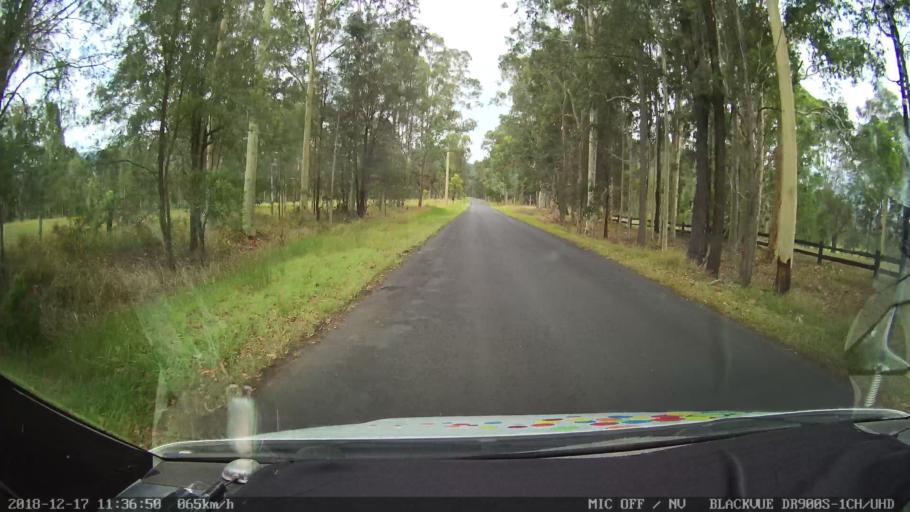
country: AU
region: New South Wales
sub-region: Kyogle
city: Kyogle
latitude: -28.7103
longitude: 152.6062
